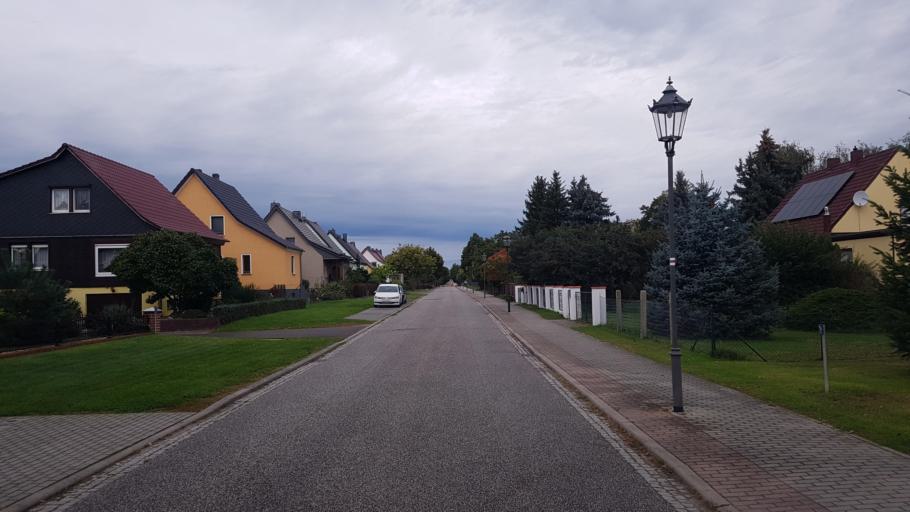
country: DE
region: Brandenburg
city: Golssen
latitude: 51.9659
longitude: 13.6135
